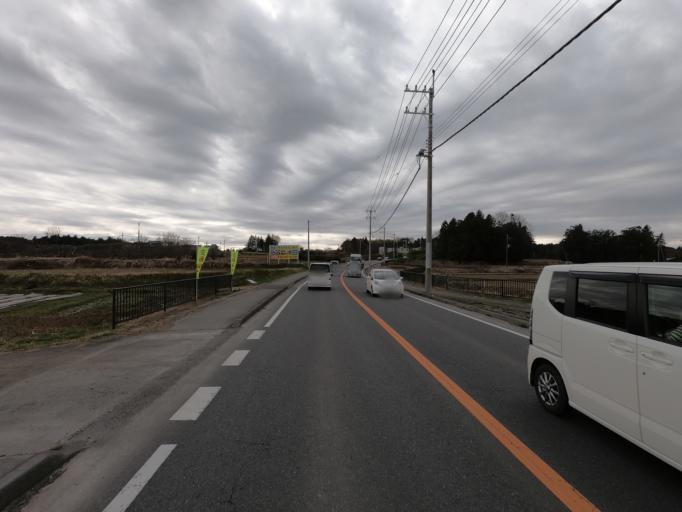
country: JP
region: Ibaraki
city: Ishioka
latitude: 36.0910
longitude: 140.3160
